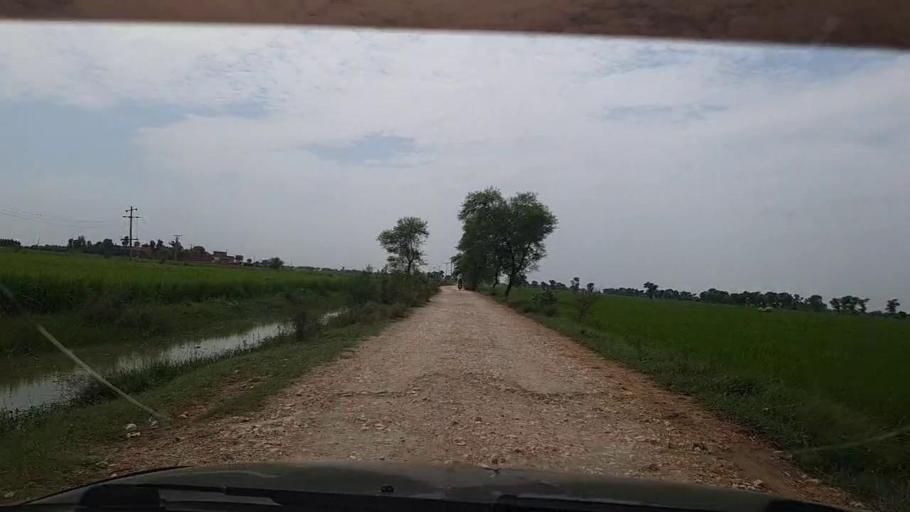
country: PK
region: Sindh
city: Thul
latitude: 28.2424
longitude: 68.7257
